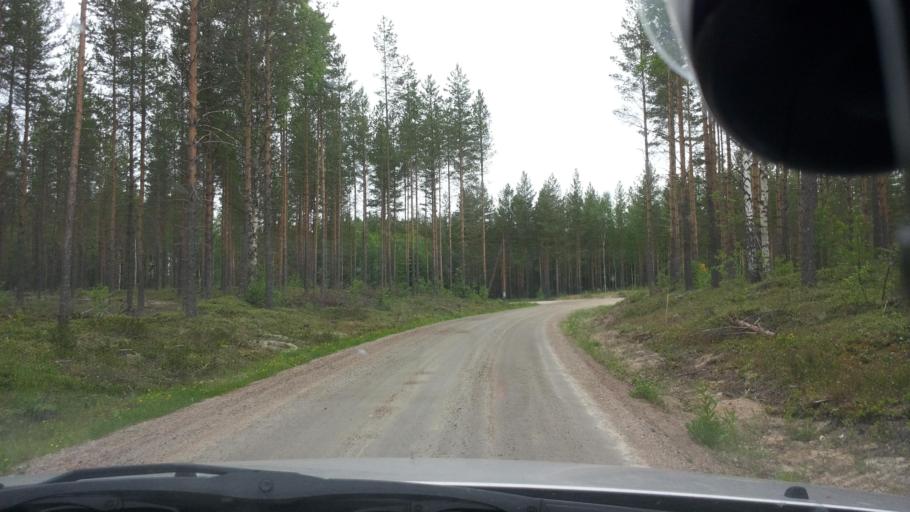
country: SE
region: Gaevleborg
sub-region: Ovanakers Kommun
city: Edsbyn
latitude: 61.5218
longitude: 15.3560
